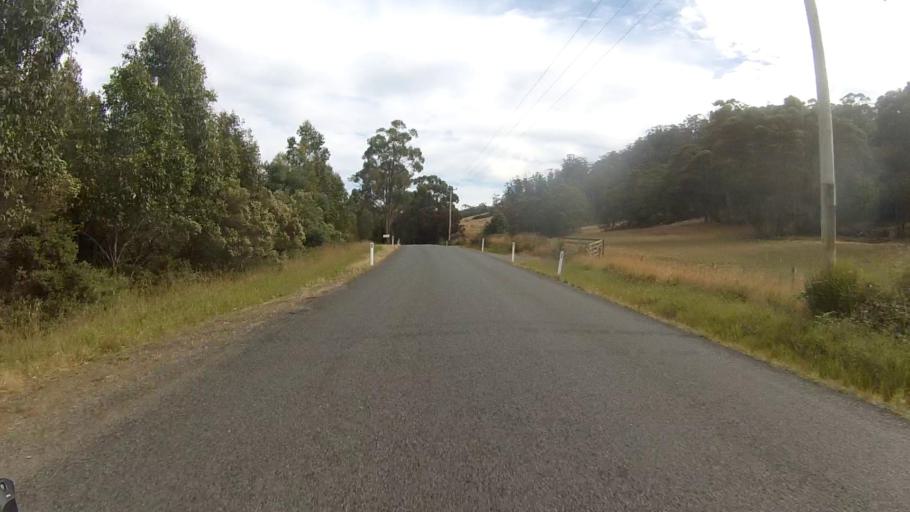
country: AU
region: Tasmania
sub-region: Sorell
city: Sorell
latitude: -42.8095
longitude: 147.7945
